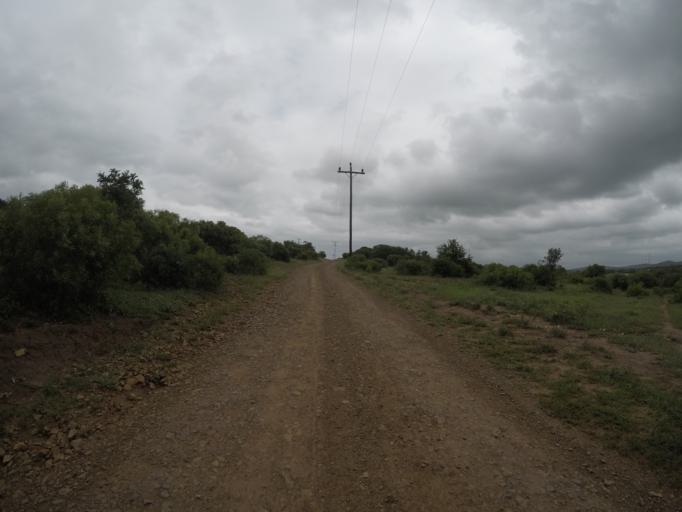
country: ZA
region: KwaZulu-Natal
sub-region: uThungulu District Municipality
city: Empangeni
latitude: -28.5963
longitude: 31.8317
